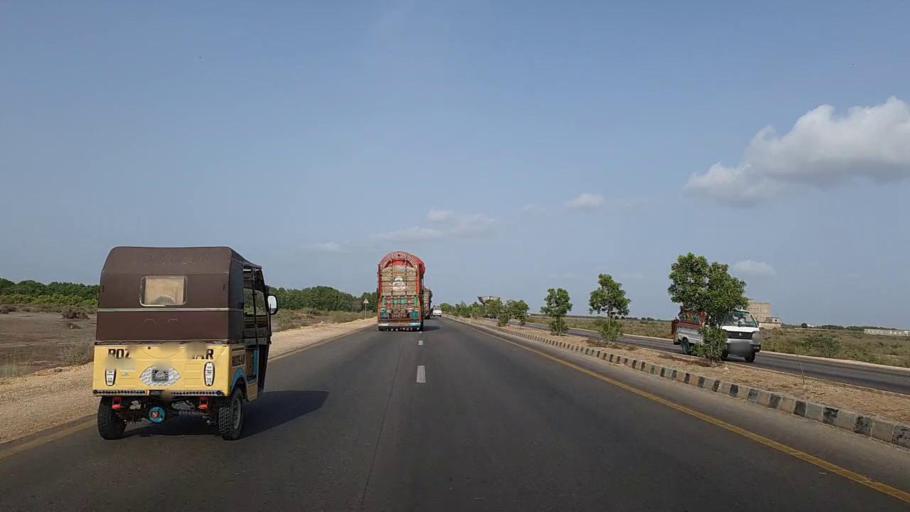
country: PK
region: Sindh
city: Gharo
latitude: 24.7376
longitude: 67.7221
